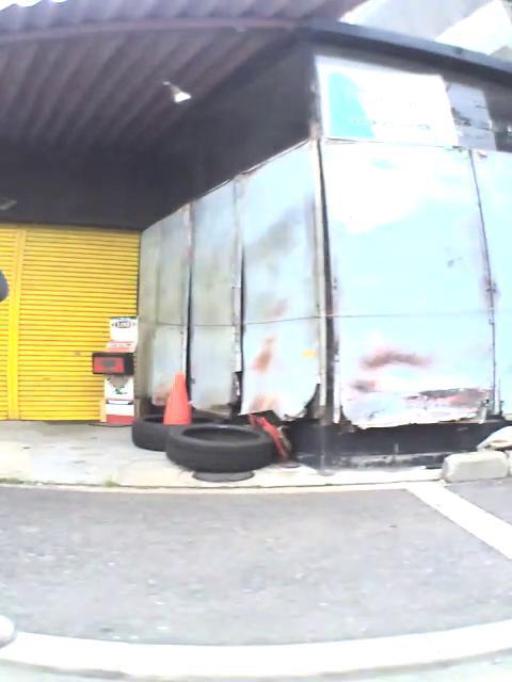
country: JP
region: Osaka
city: Neyagawa
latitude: 34.7535
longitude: 135.6255
